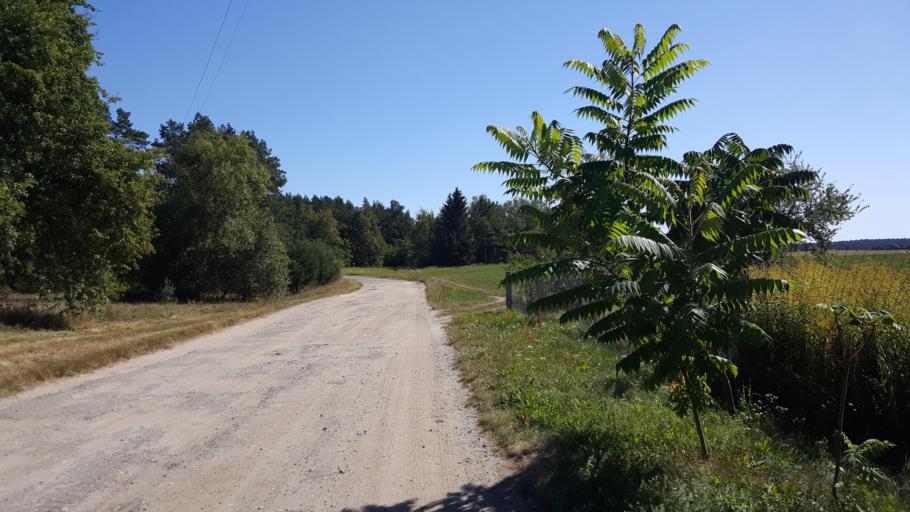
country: BY
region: Brest
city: Vysokaye
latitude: 52.2331
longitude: 23.5047
